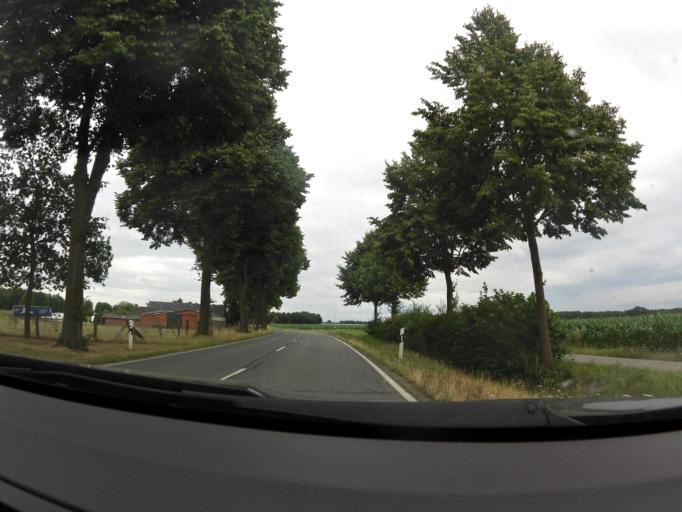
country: DE
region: North Rhine-Westphalia
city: Geldern
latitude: 51.5249
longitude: 6.2662
